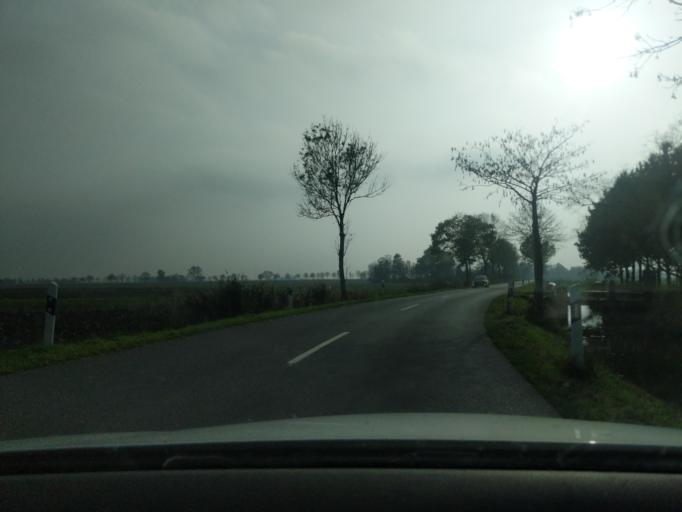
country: DE
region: Lower Saxony
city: Ihlienworth
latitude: 53.7288
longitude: 8.9366
